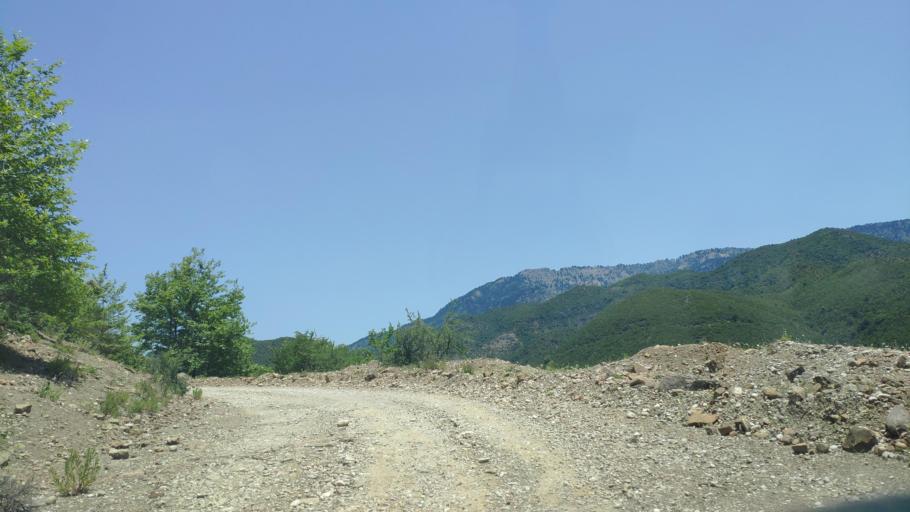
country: GR
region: Thessaly
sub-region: Nomos Kardhitsas
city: Anthiro
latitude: 39.1737
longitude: 21.3701
